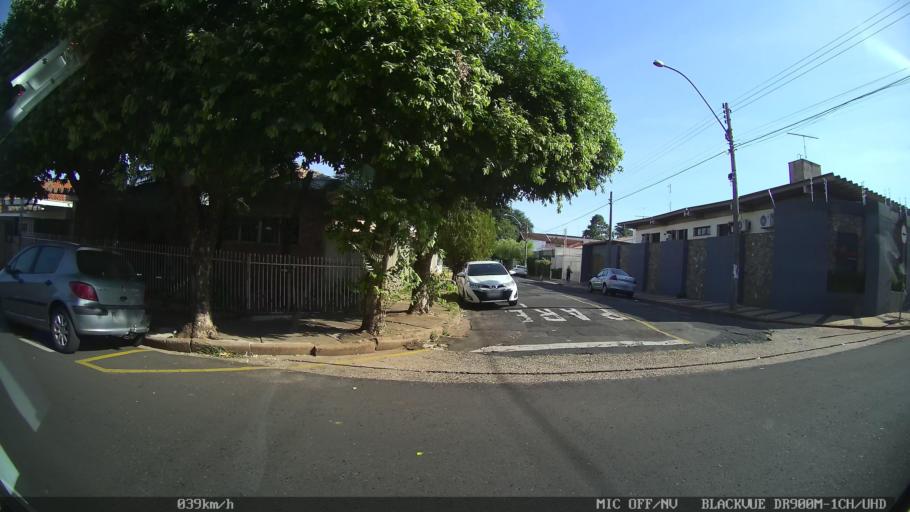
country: BR
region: Sao Paulo
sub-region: Sao Jose Do Rio Preto
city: Sao Jose do Rio Preto
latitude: -20.8092
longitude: -49.3912
